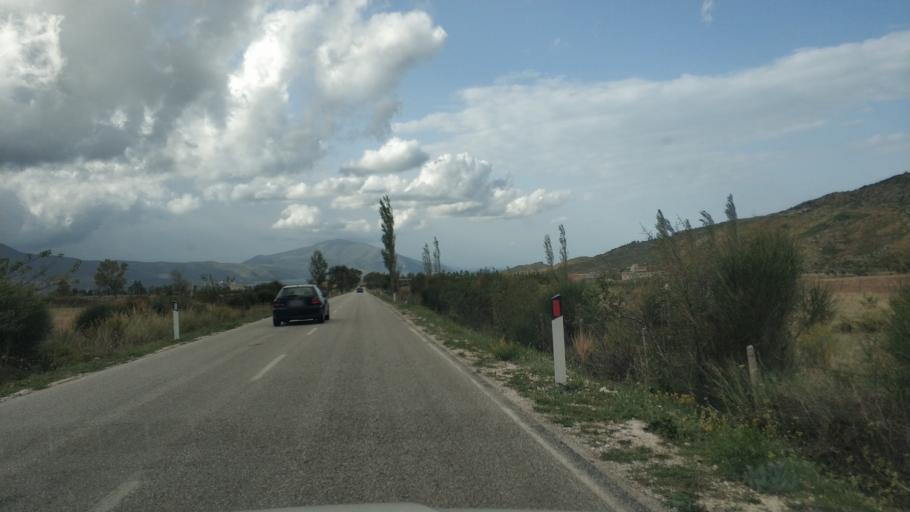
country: AL
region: Vlore
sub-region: Rrethi i Vlores
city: Orikum
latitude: 40.2744
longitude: 19.5092
